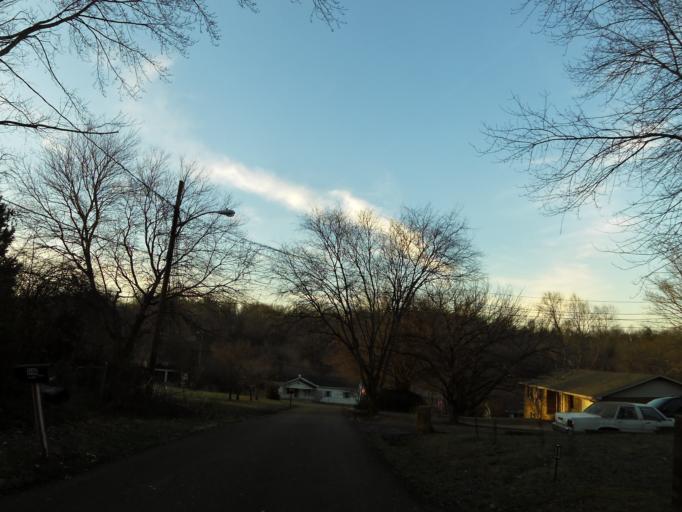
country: US
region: Tennessee
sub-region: Knox County
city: Knoxville
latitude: 36.0206
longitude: -83.8671
